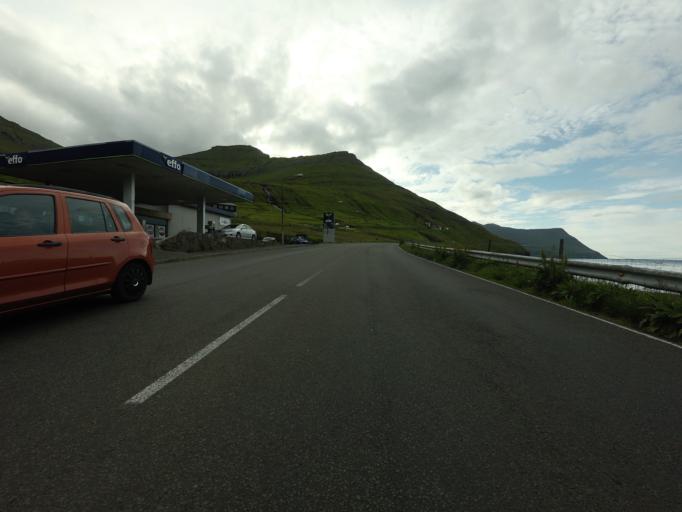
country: FO
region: Eysturoy
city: Eystur
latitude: 62.2133
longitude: -6.7135
